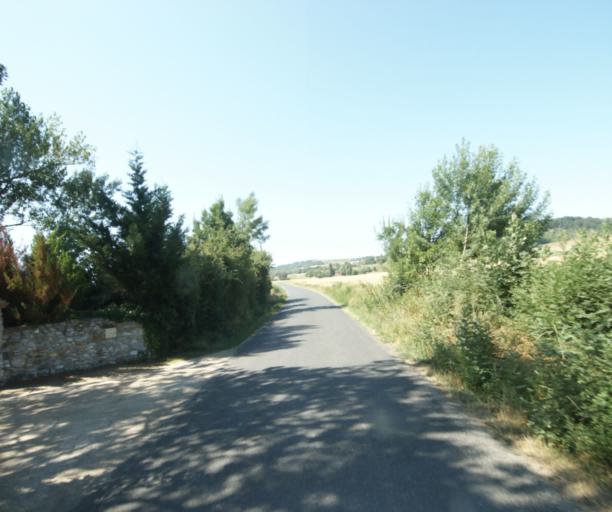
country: FR
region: Midi-Pyrenees
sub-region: Departement de la Haute-Garonne
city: Revel
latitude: 43.5143
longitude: 1.9568
